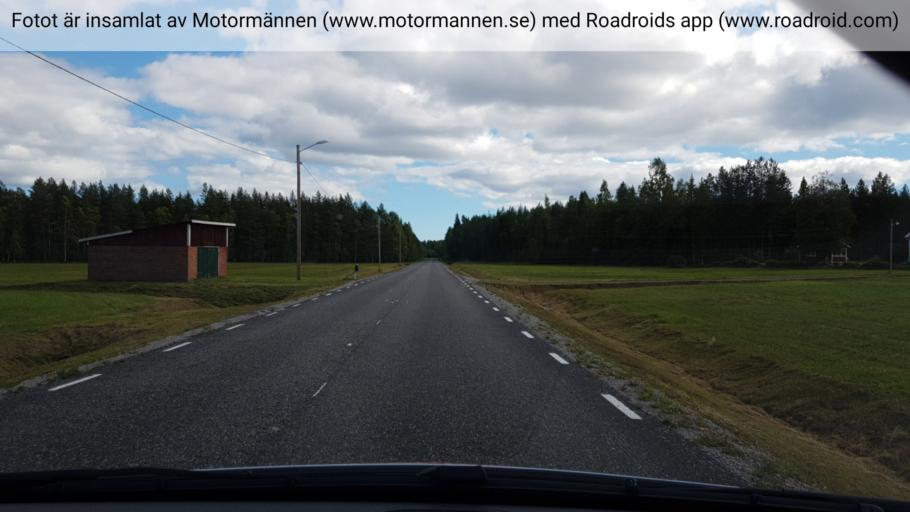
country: SE
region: Vaesterbotten
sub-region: Umea Kommun
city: Hoernefors
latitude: 63.6906
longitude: 19.8561
